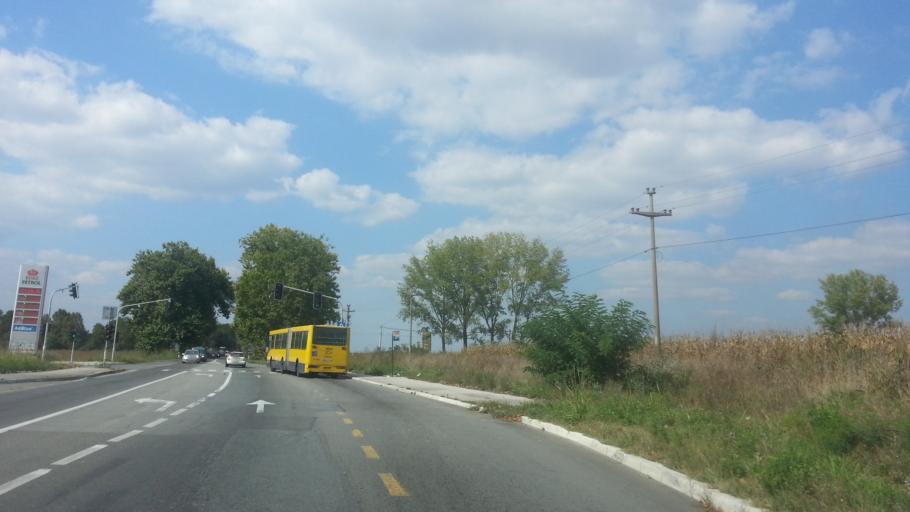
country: RS
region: Central Serbia
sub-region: Belgrade
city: Zemun
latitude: 44.8780
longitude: 20.3344
